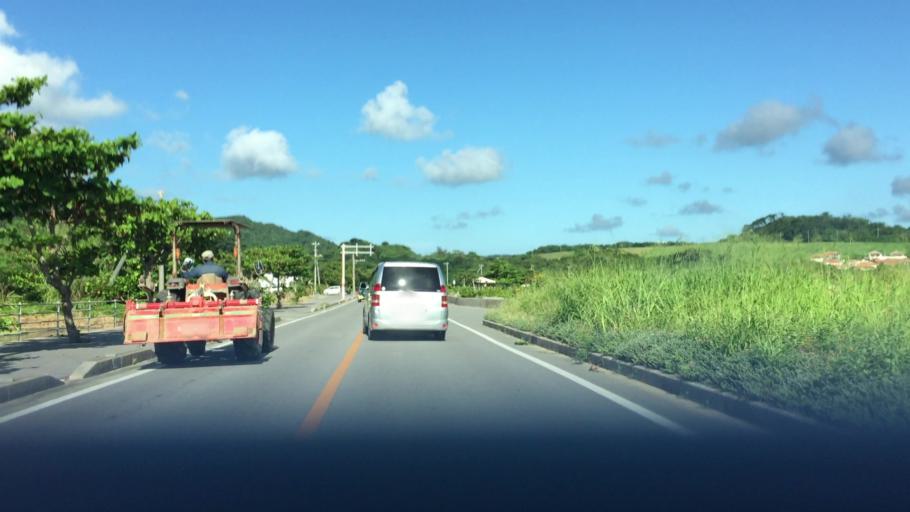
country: JP
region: Okinawa
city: Ishigaki
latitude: 24.4149
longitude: 124.1397
